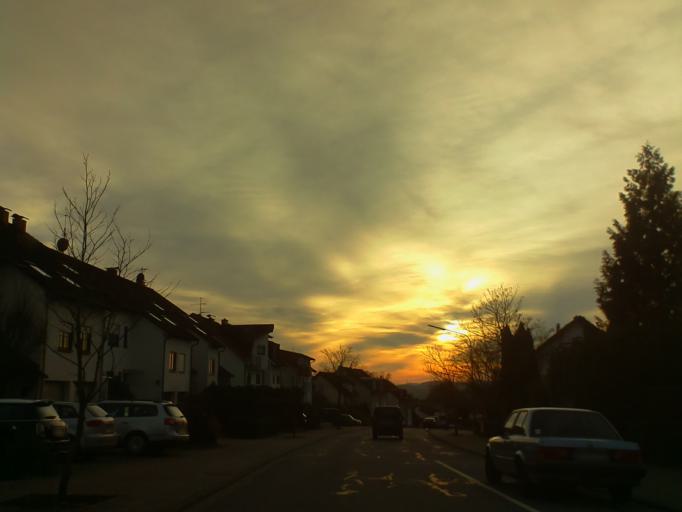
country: DE
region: Hesse
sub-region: Regierungsbezirk Darmstadt
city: Furth
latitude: 49.6463
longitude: 8.7811
